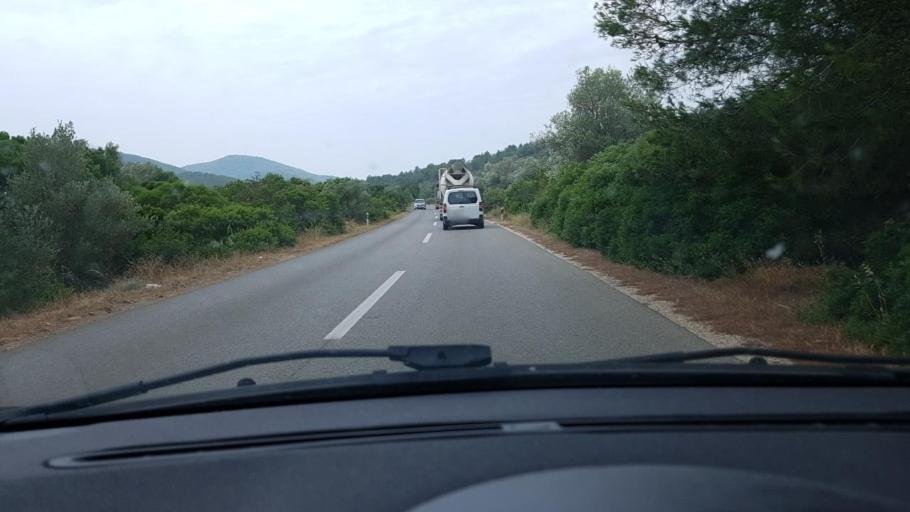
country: HR
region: Dubrovacko-Neretvanska
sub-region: Grad Dubrovnik
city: Vela Luka
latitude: 42.9503
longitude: 16.7561
